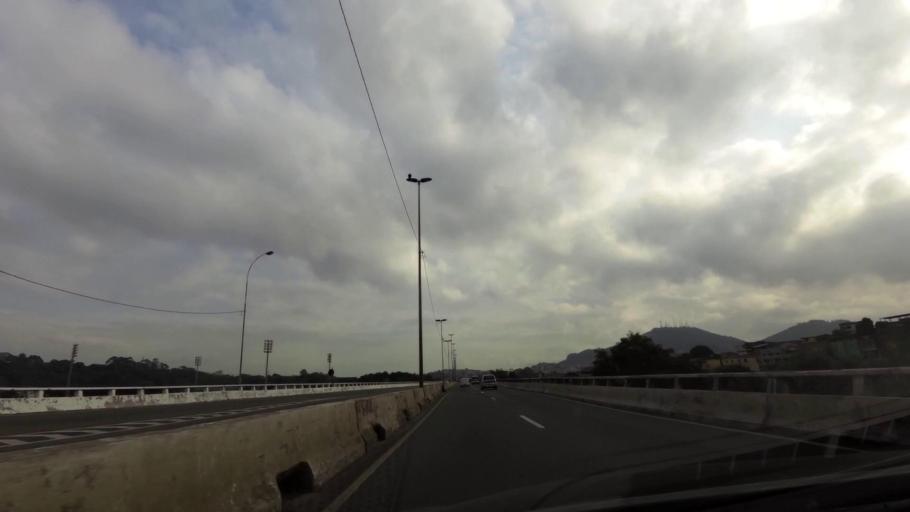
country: BR
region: Espirito Santo
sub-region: Vitoria
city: Vitoria
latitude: -20.3367
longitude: -40.3547
